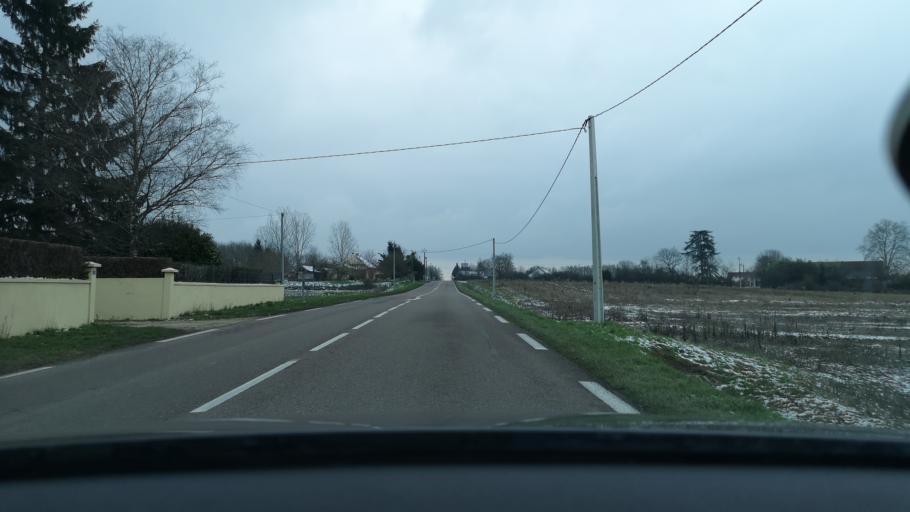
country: FR
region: Bourgogne
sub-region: Departement de Saone-et-Loire
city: Ouroux-sur-Saone
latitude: 46.7587
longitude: 4.9975
